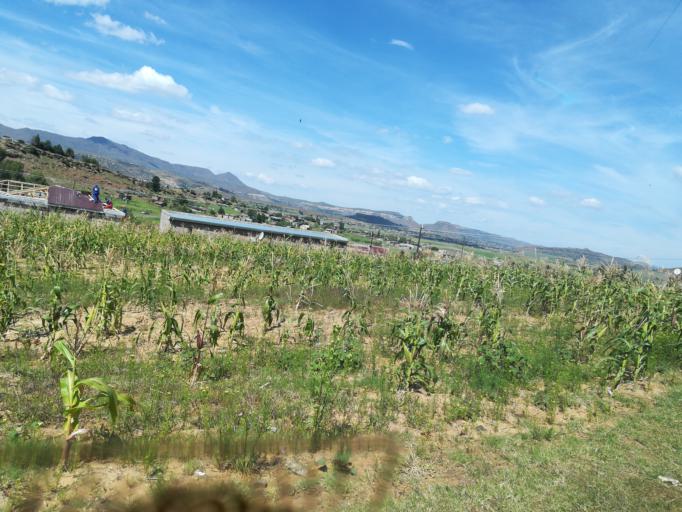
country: LS
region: Mohale's Hoek District
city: Mohale's Hoek
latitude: -30.1023
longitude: 27.4761
